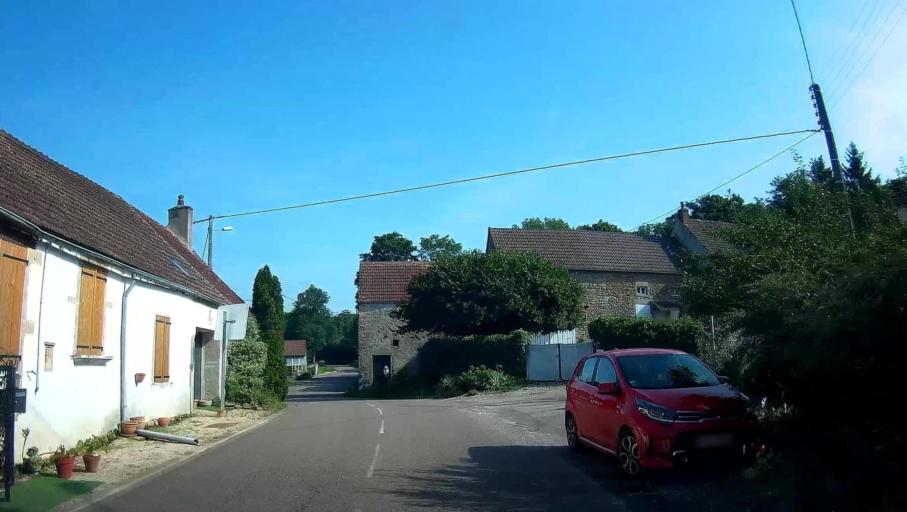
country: FR
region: Bourgogne
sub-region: Departement de Saone-et-Loire
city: Couches
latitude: 46.8912
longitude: 4.5986
